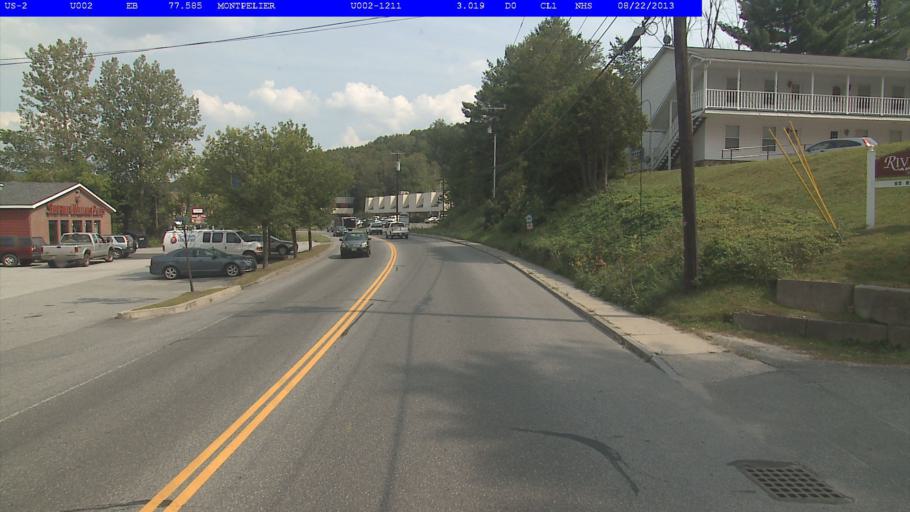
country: US
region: Vermont
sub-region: Washington County
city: Montpelier
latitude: 44.2491
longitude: -72.5658
